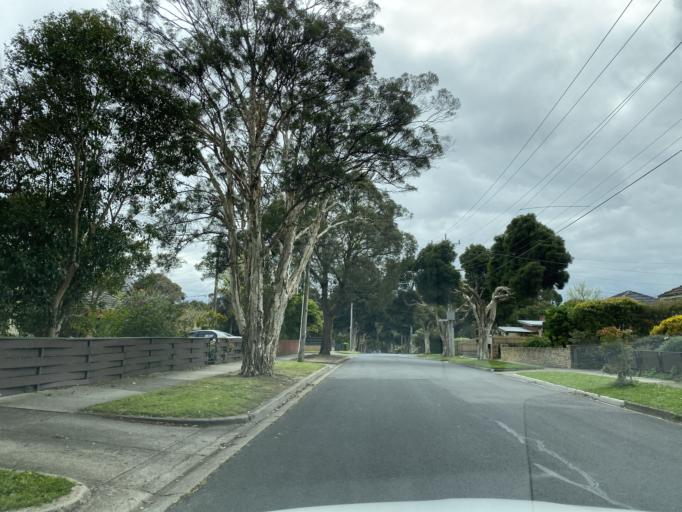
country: AU
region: Victoria
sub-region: Whitehorse
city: Burwood
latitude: -37.8441
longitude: 145.1292
